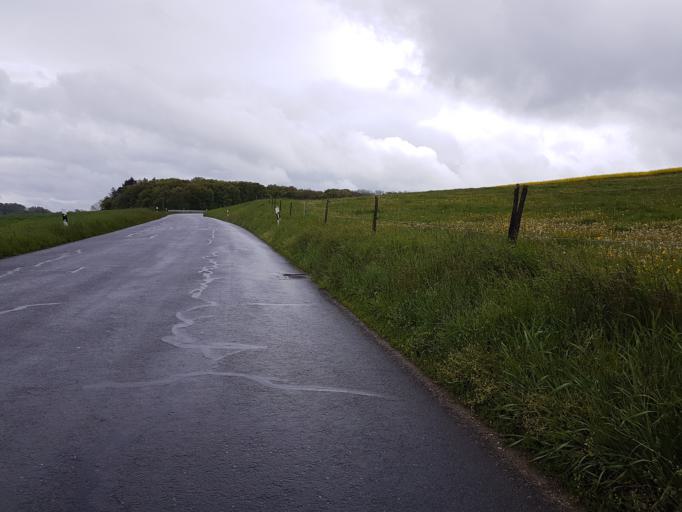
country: CH
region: Vaud
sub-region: Morges District
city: Orny
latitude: 46.6450
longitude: 6.5320
